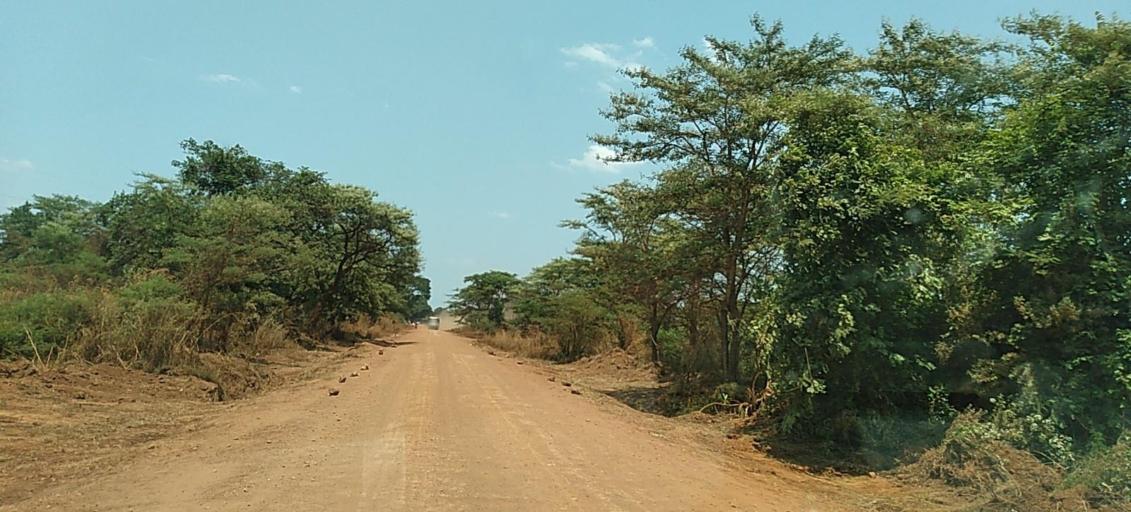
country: ZM
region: Copperbelt
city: Mpongwe
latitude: -13.5139
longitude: 28.0316
